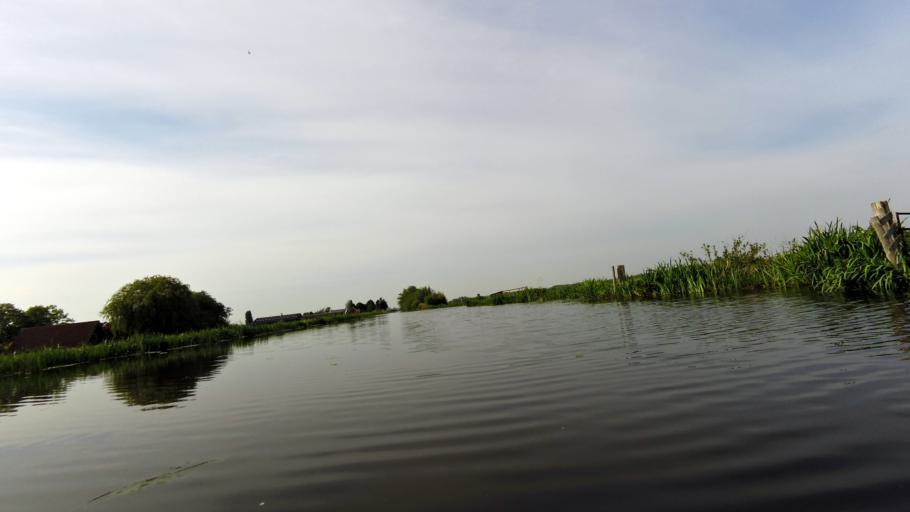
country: NL
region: South Holland
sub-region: Bodegraven-Reeuwijk
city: Reeuwijk
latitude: 52.0717
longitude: 4.7186
